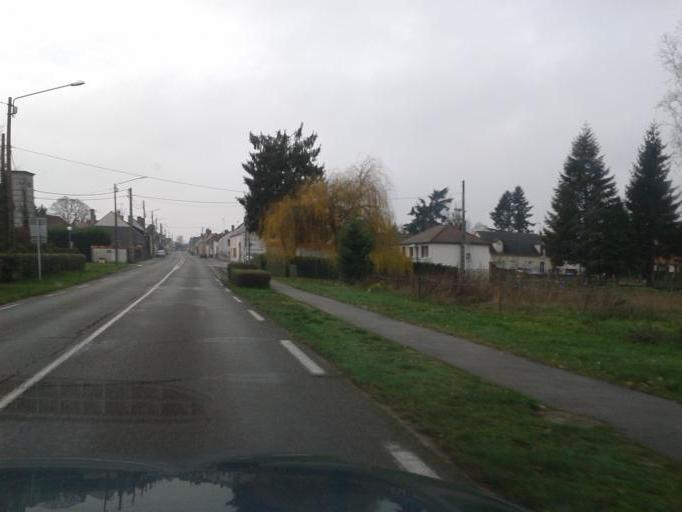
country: FR
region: Centre
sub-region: Departement du Loiret
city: Lailly-en-Val
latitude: 47.7601
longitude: 1.6773
